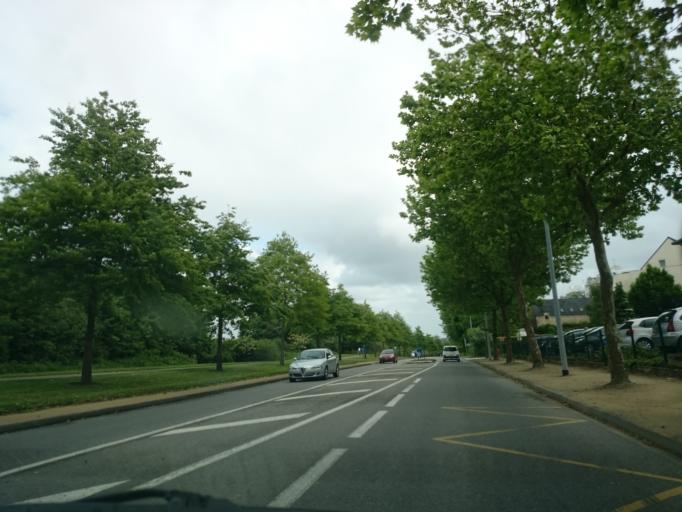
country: FR
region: Brittany
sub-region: Departement du Morbihan
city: Vannes
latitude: 47.6671
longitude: -2.7745
